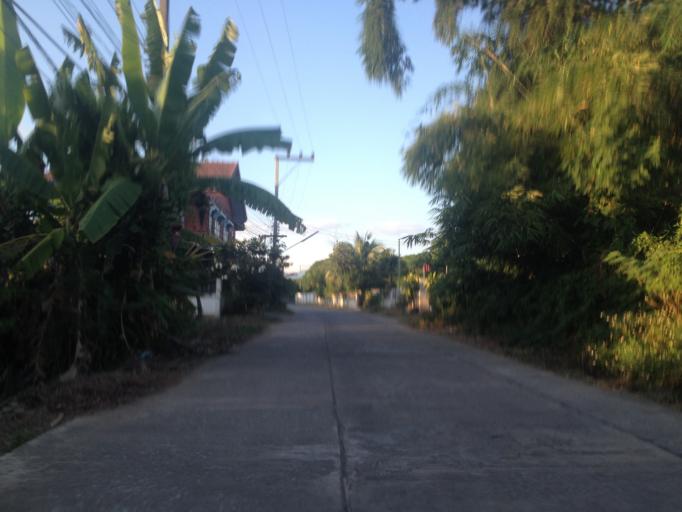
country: TH
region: Chiang Mai
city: San Pa Tong
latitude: 18.6492
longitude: 98.8863
